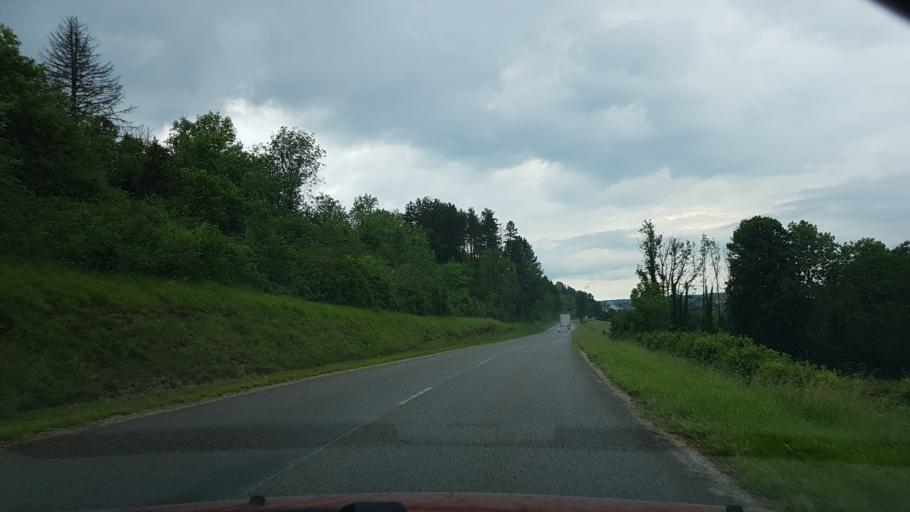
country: FR
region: Franche-Comte
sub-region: Departement du Jura
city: Clairvaux-les-Lacs
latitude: 46.5631
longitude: 5.7438
